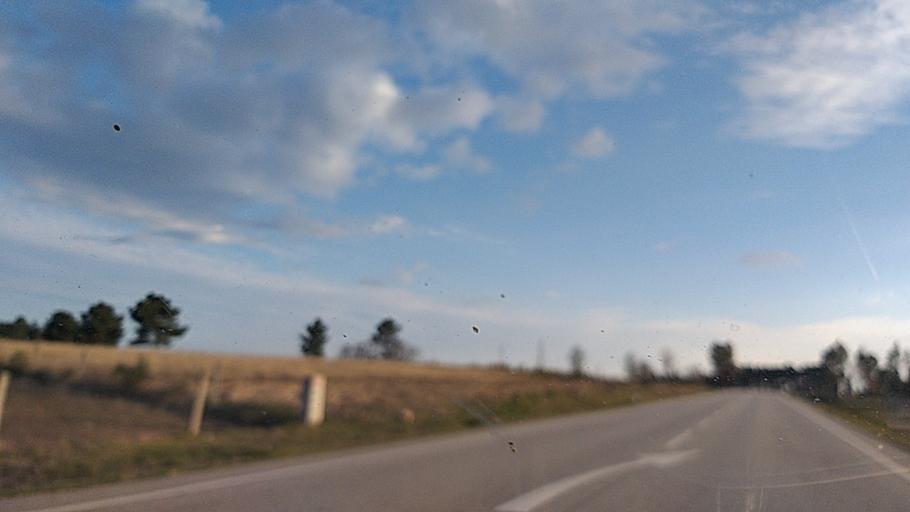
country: PT
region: Guarda
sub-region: Pinhel
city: Pinhel
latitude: 40.6460
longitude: -6.9682
